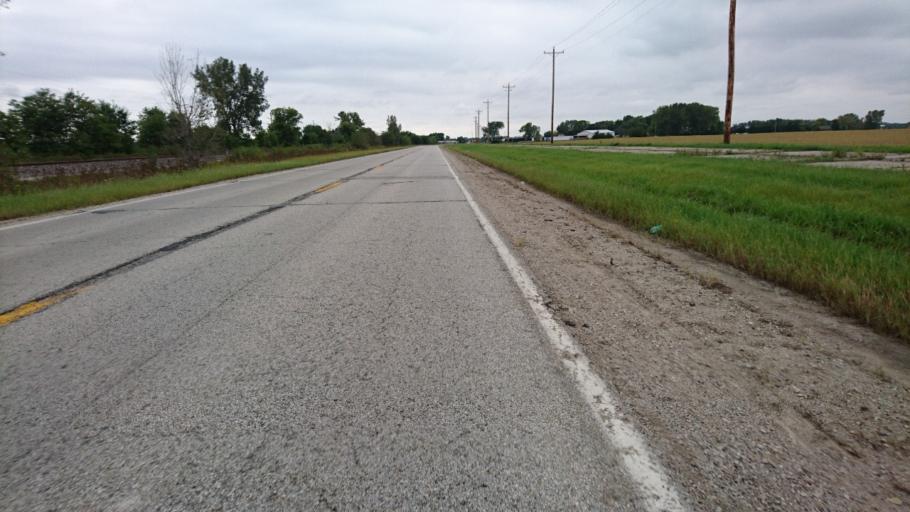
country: US
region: Illinois
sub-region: Livingston County
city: Pontiac
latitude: 40.9039
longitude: -88.6180
